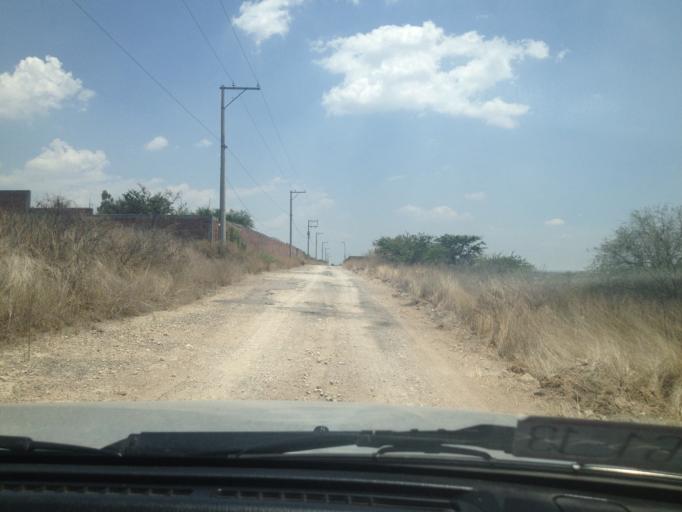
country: MX
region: Aguascalientes
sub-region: Aguascalientes
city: San Sebastian [Fraccionamiento]
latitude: 21.7893
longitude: -102.3363
